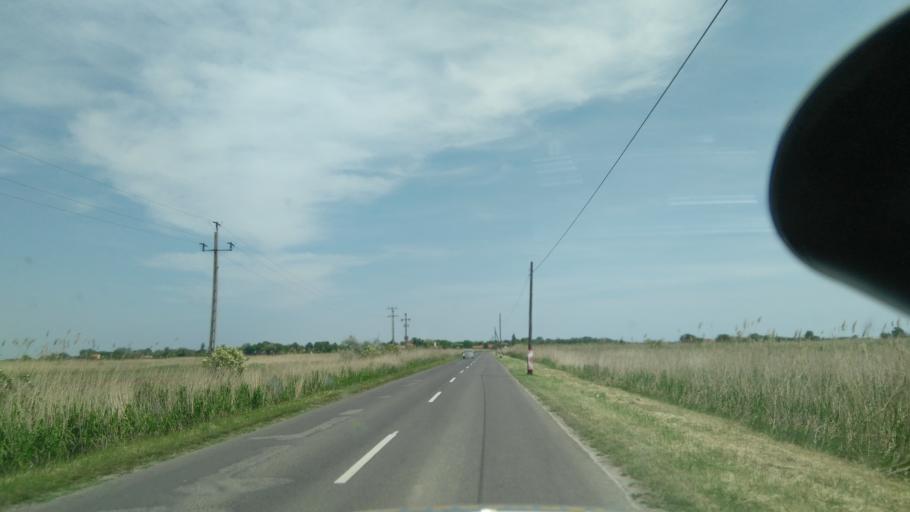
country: HU
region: Csongrad
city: Szekkutas
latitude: 46.5678
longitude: 20.5825
